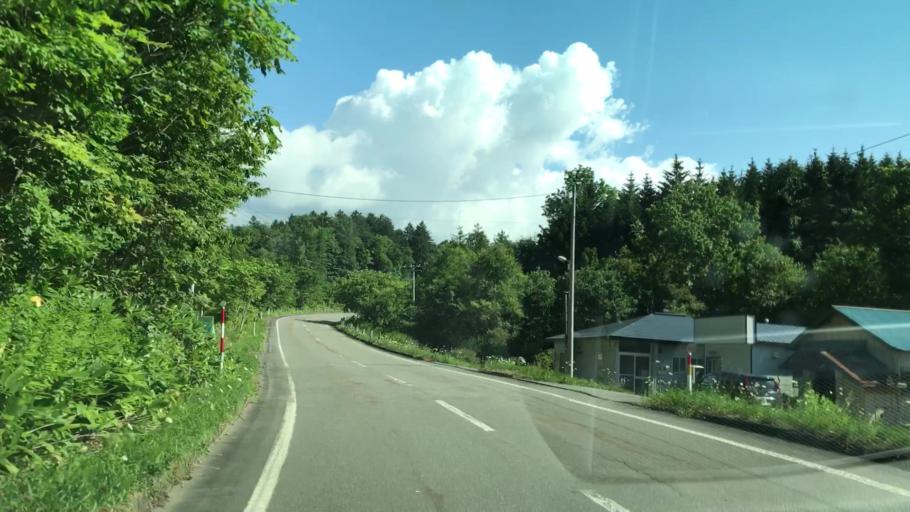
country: JP
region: Hokkaido
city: Shimo-furano
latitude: 42.8643
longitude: 142.4400
